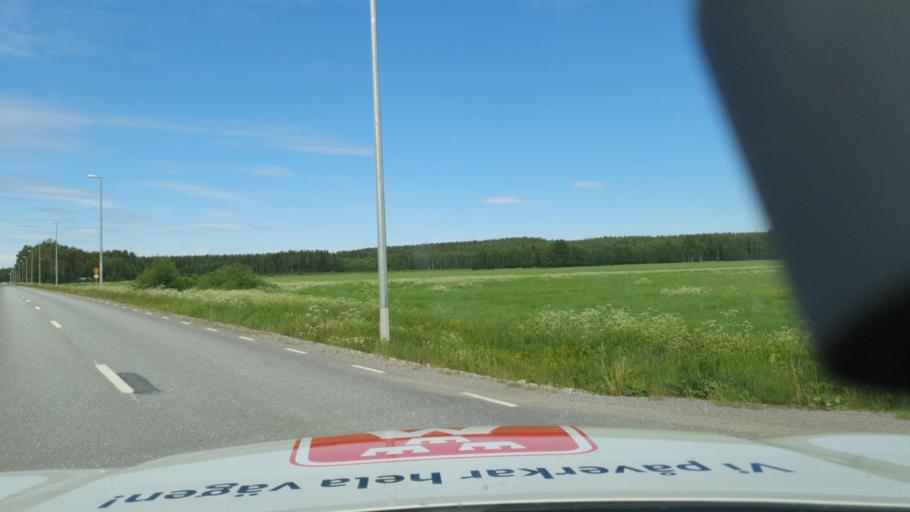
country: SE
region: Vaesterbotten
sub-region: Skelleftea Kommun
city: Forsbacka
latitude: 64.6864
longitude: 20.5249
